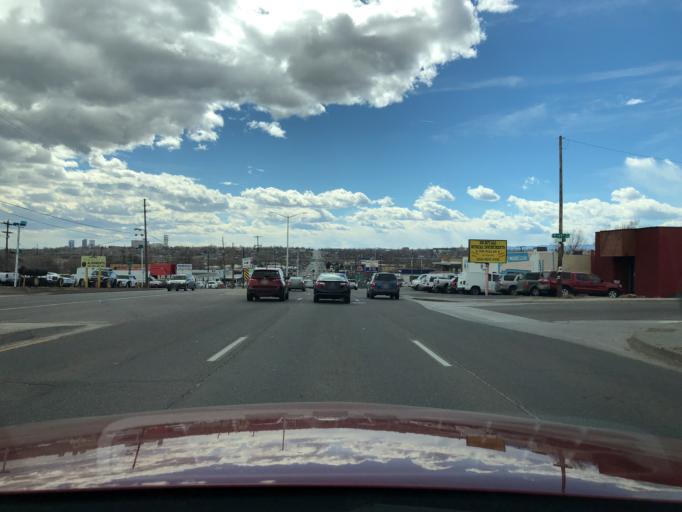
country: US
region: Colorado
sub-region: Adams County
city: Berkley
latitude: 39.8151
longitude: -105.0253
